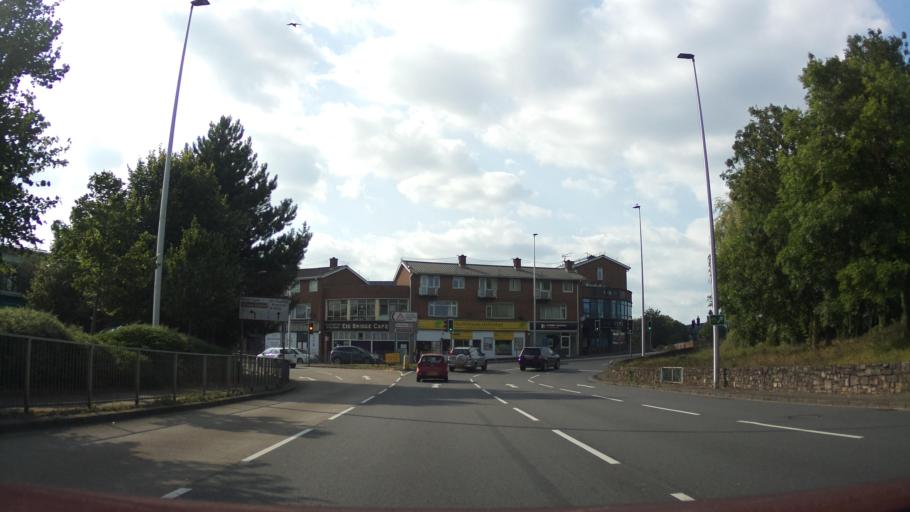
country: GB
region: England
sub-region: Devon
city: Exeter
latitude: 50.7177
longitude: -3.5374
